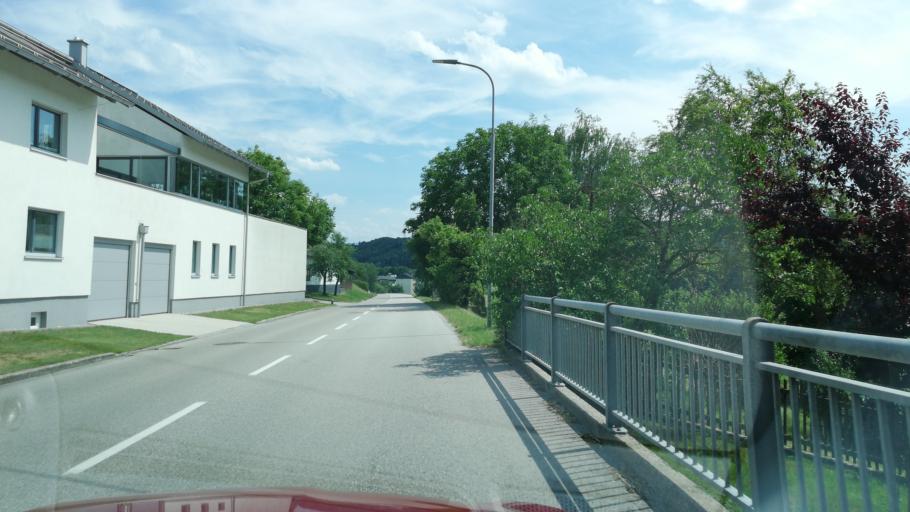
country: AT
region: Upper Austria
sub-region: Politischer Bezirk Vocklabruck
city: Vocklabruck
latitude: 48.0003
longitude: 13.6335
